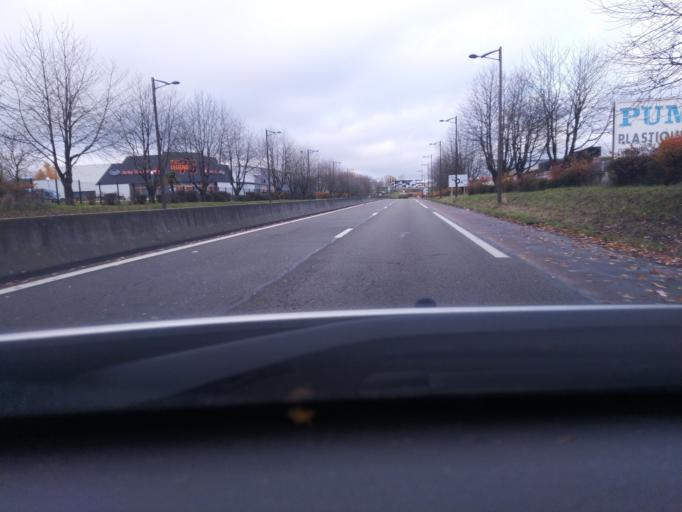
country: FR
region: Haute-Normandie
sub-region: Departement de la Seine-Maritime
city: Maromme
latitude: 49.4861
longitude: 1.0162
